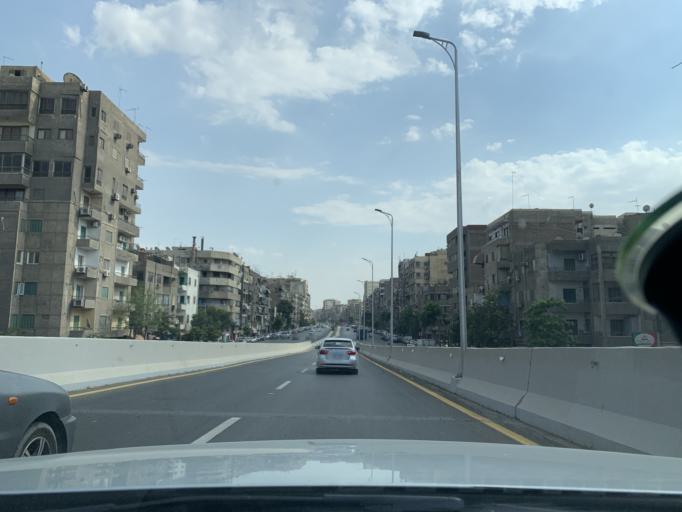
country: EG
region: Muhafazat al Qalyubiyah
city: Al Khankah
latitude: 30.1103
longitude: 31.3453
